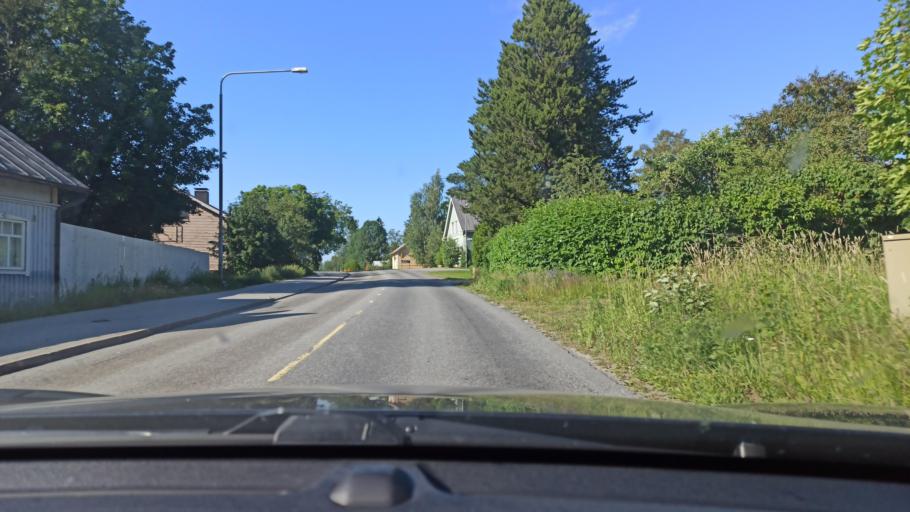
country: FI
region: Satakunta
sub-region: Pori
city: Noormarkku
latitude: 61.5114
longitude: 21.8672
